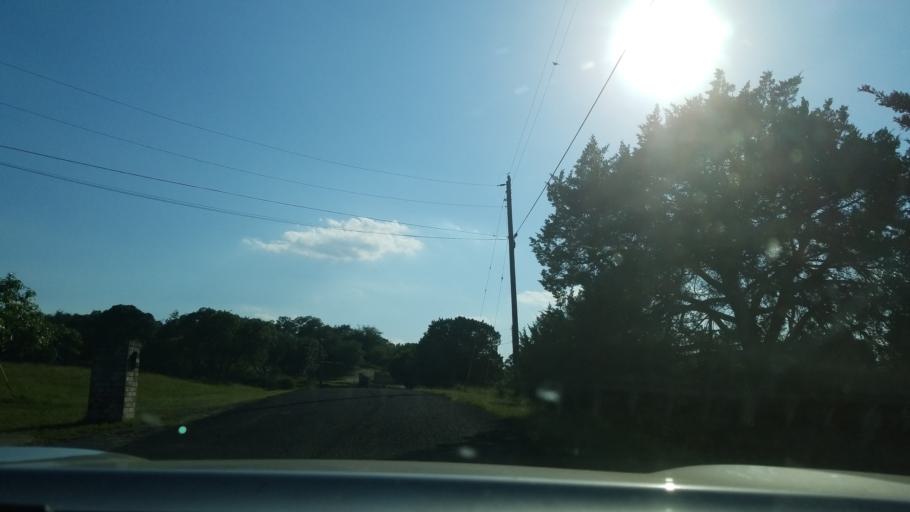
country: US
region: Texas
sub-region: Comal County
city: Bulverde
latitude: 29.7828
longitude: -98.4438
